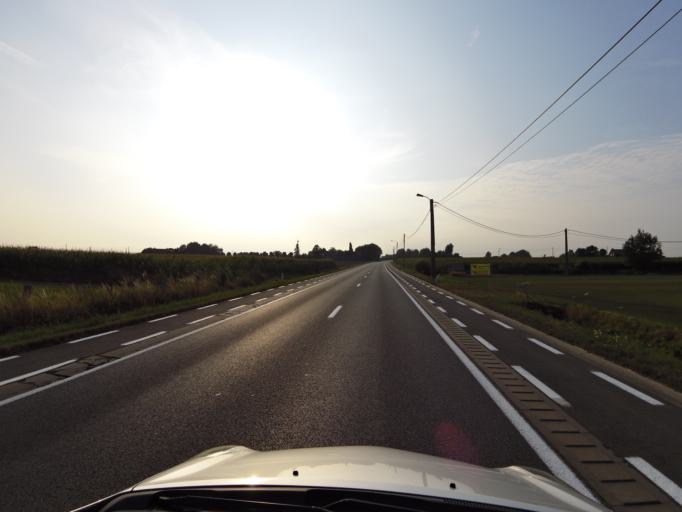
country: BE
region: Flanders
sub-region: Provincie West-Vlaanderen
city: Ardooie
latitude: 51.0044
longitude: 3.1872
